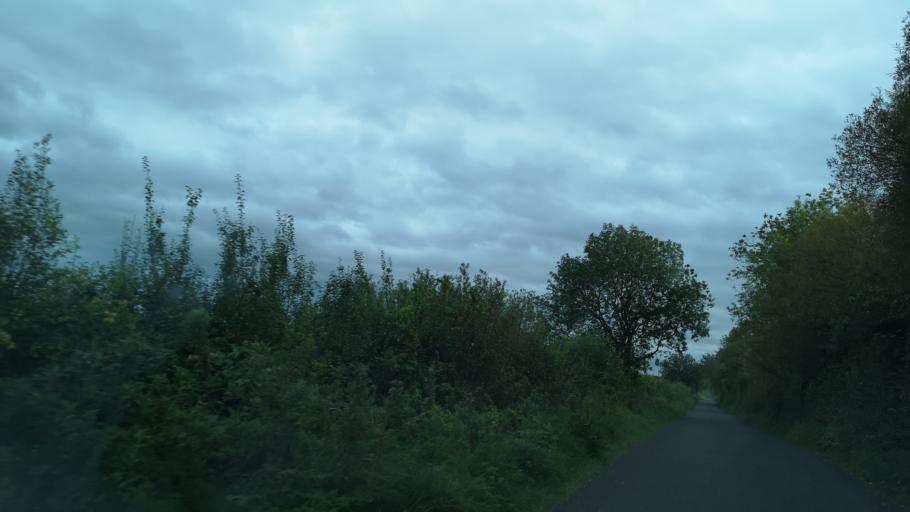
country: IE
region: Leinster
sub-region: Uibh Fhaili
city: Ferbane
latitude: 53.1899
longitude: -7.7265
